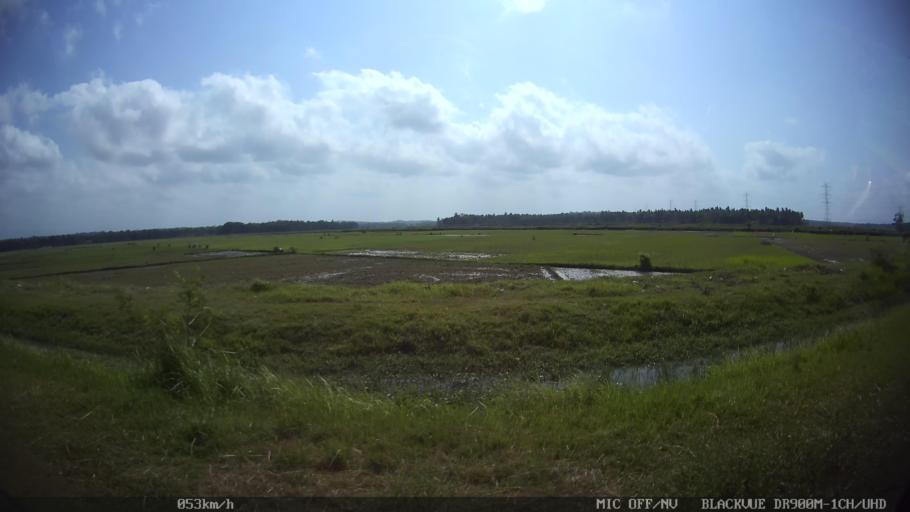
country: ID
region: Daerah Istimewa Yogyakarta
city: Srandakan
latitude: -7.9162
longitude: 110.1799
